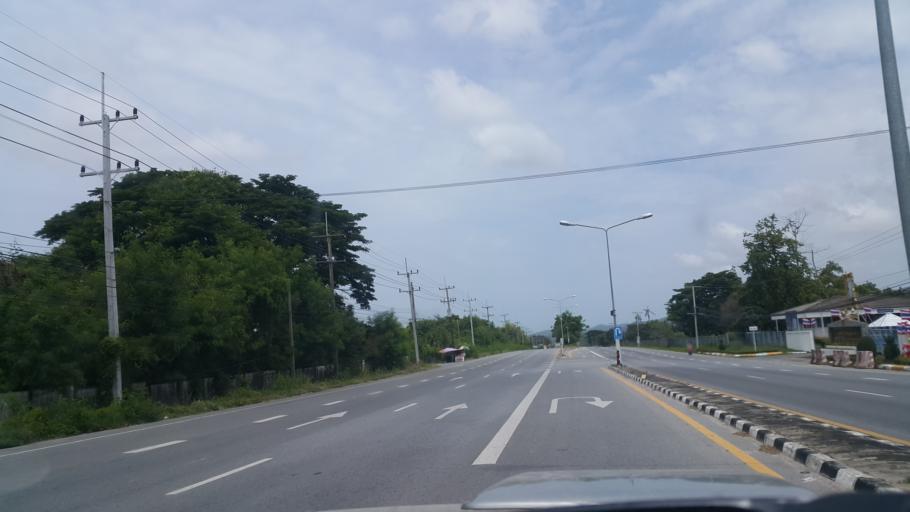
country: TH
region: Rayong
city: Ban Chang
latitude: 12.7068
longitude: 101.0206
